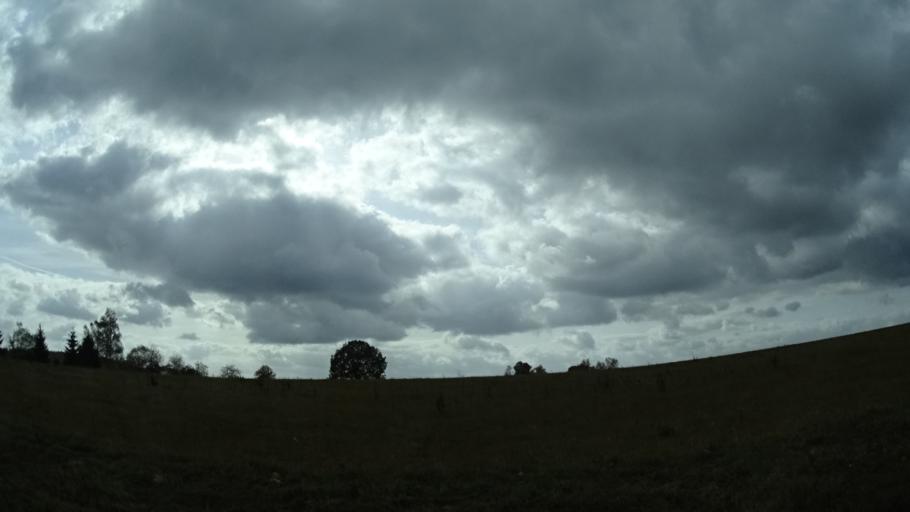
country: DE
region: Thuringia
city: Rotterode
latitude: 50.7147
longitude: 10.5437
